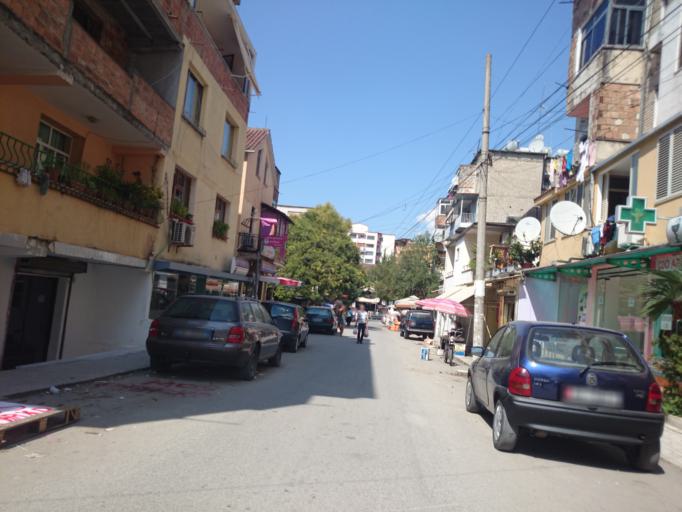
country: AL
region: Tirane
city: Tirana
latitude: 41.3245
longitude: 19.8290
